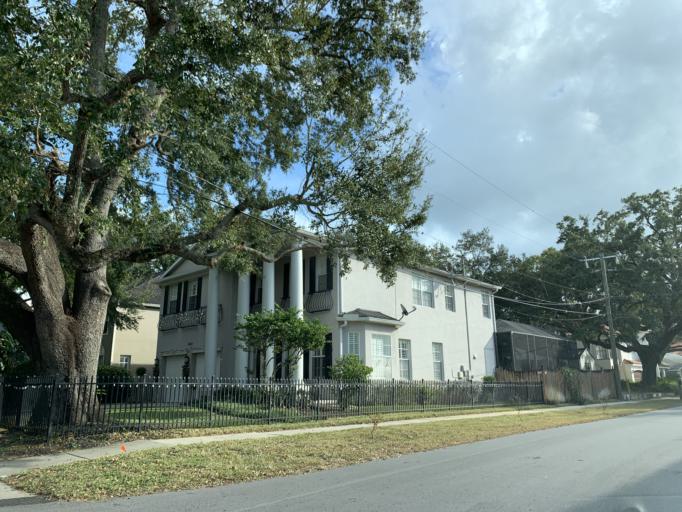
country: US
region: Florida
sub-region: Hillsborough County
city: Tampa
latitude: 27.9078
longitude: -82.4992
